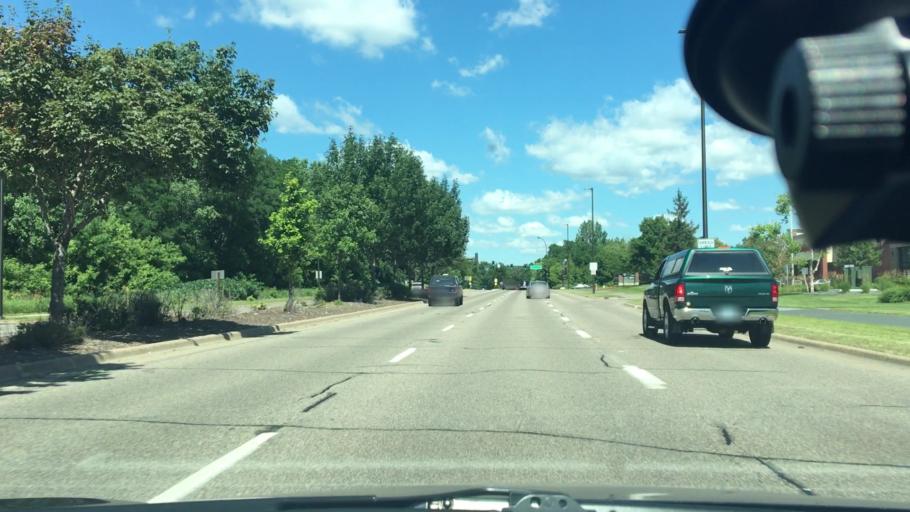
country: US
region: Minnesota
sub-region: Hennepin County
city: Maple Grove
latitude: 45.0682
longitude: -93.4499
